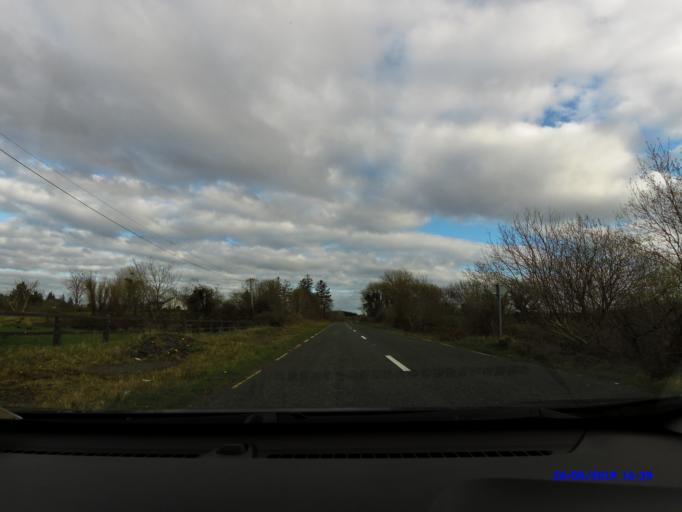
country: IE
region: Connaught
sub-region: Maigh Eo
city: Ballyhaunis
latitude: 53.8844
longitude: -8.7962
